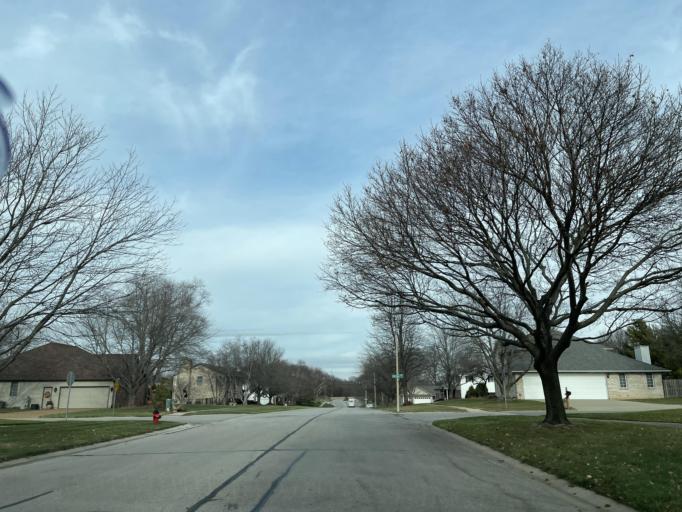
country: US
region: Illinois
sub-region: Sangamon County
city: Leland Grove
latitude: 39.7836
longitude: -89.7288
